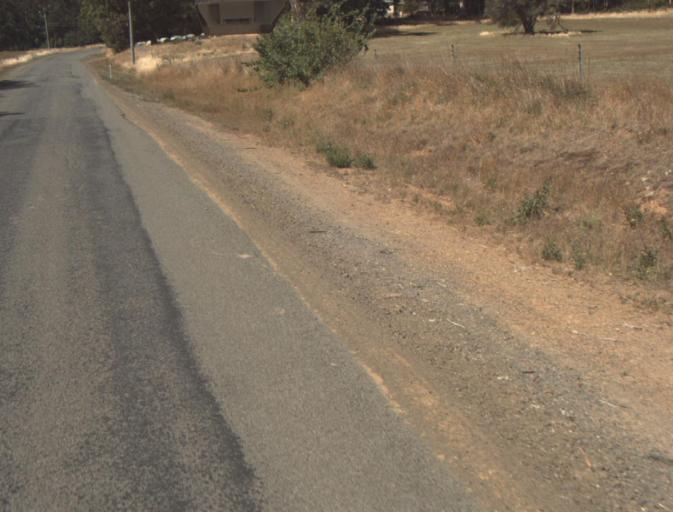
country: AU
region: Tasmania
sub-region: Dorset
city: Scottsdale
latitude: -41.3113
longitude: 147.3905
